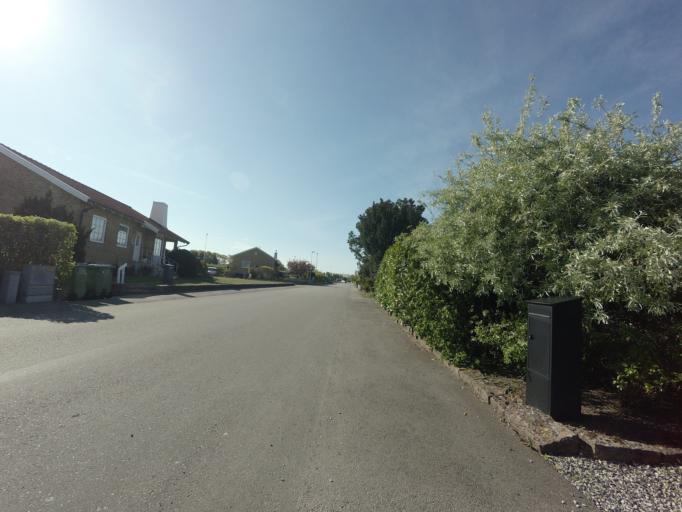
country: SE
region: Skane
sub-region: Hoganas Kommun
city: Hoganas
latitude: 56.2419
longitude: 12.5409
